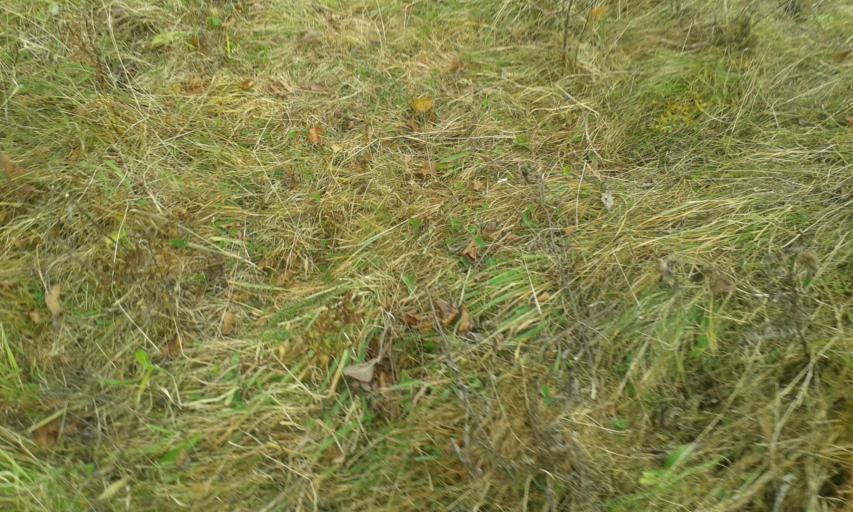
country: RO
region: Hunedoara
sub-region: Comuna Aninoasa
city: Iscroni
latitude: 45.3720
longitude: 23.3875
